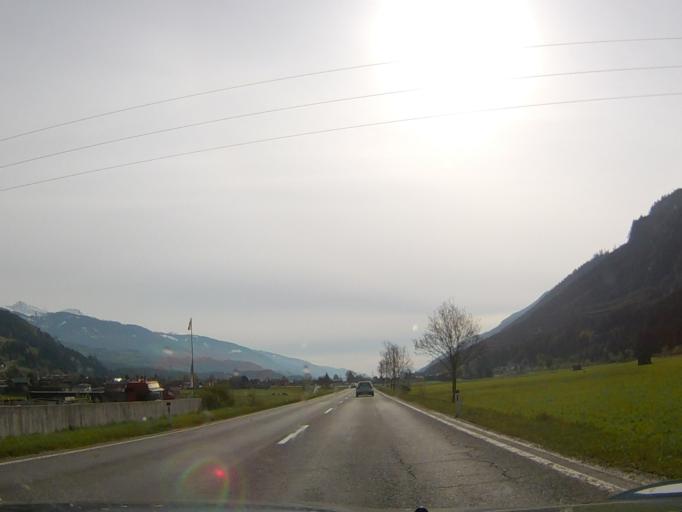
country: AT
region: Salzburg
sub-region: Politischer Bezirk Zell am See
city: Bramberg am Wildkogel
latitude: 47.2727
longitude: 12.3537
